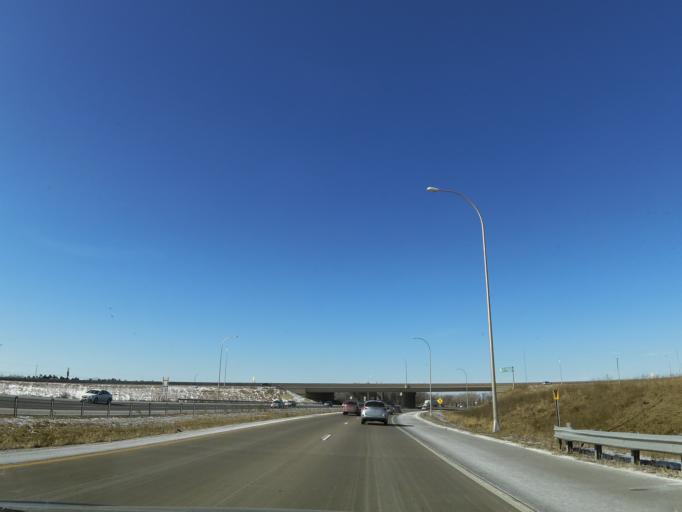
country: US
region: Minnesota
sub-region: Ramsey County
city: Arden Hills
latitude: 45.0612
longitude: -93.1554
